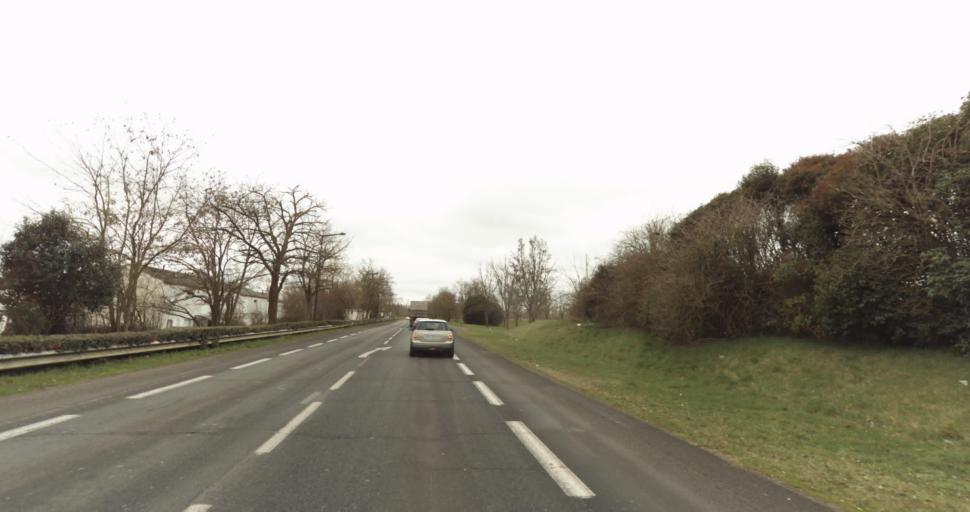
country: FR
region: Pays de la Loire
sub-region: Departement de Maine-et-Loire
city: Saumur
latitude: 47.2443
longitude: -0.0793
